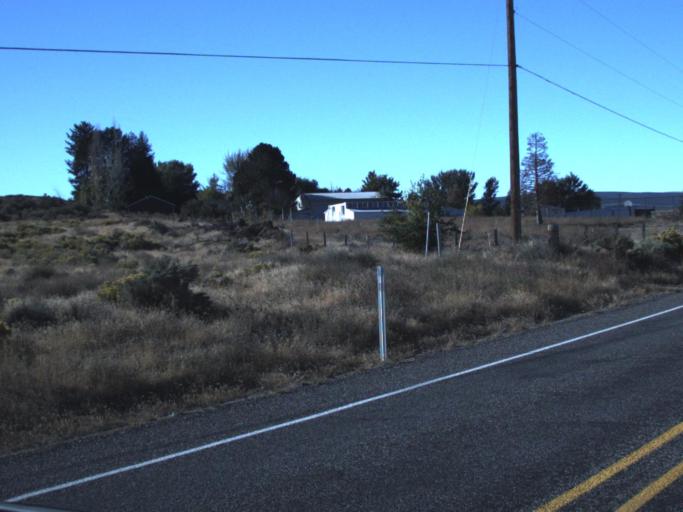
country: US
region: Washington
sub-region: Benton County
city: West Richland
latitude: 46.2990
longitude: -119.3827
